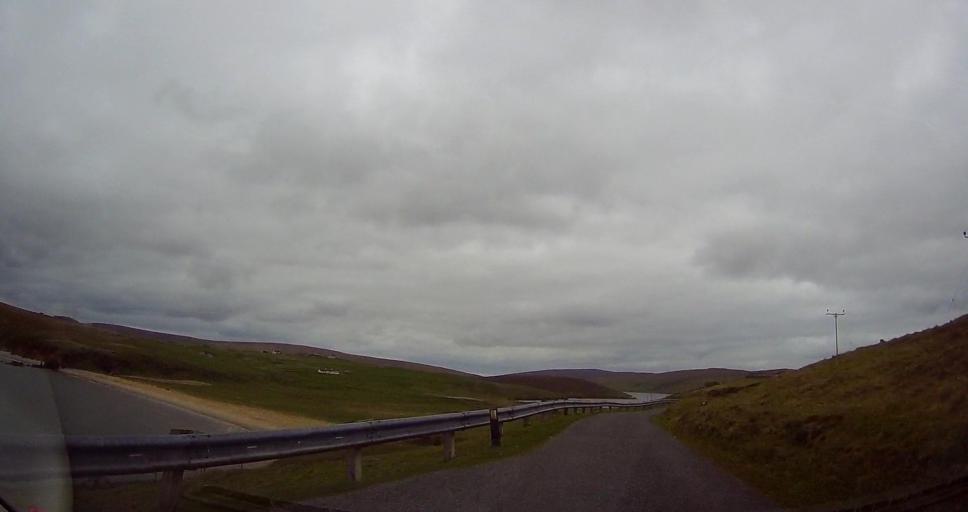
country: GB
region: Scotland
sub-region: Shetland Islands
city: Shetland
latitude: 60.8089
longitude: -0.8788
